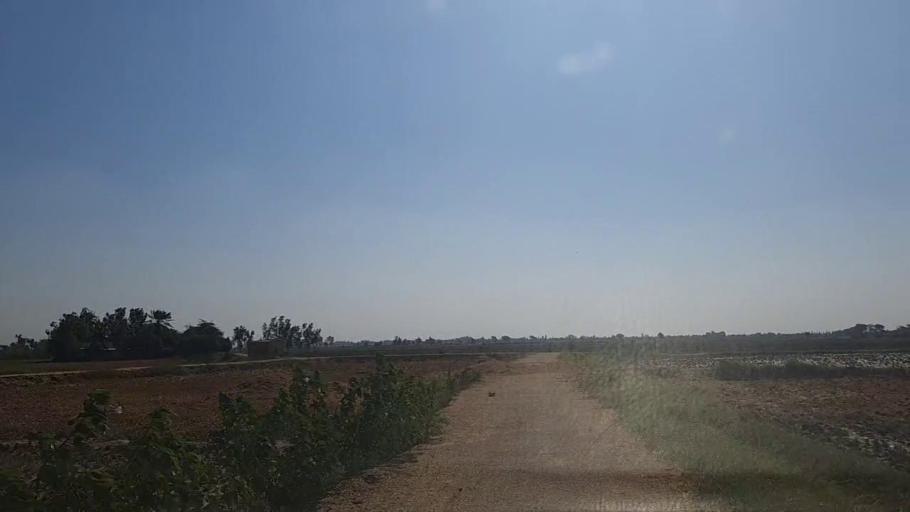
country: PK
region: Sindh
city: Thatta
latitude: 24.7705
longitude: 67.9510
